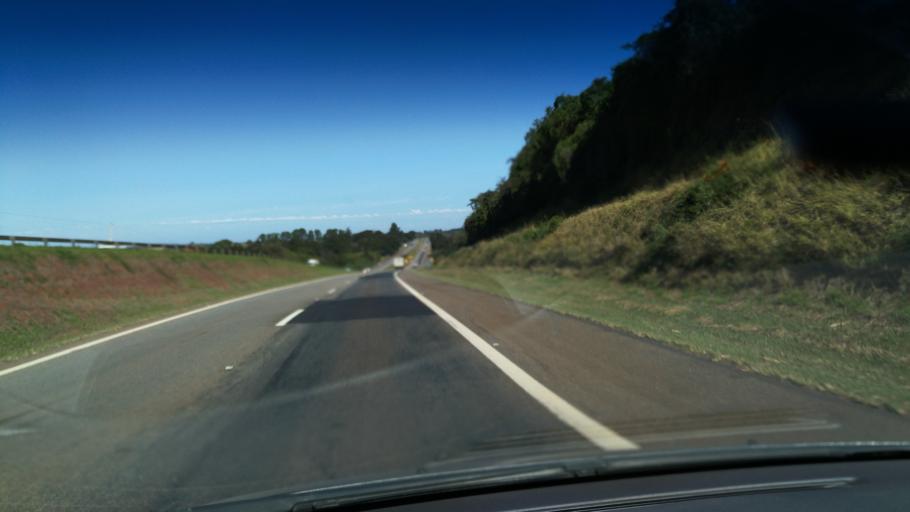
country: BR
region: Sao Paulo
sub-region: Santo Antonio De Posse
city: Santo Antonio de Posse
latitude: -22.5538
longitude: -46.9990
